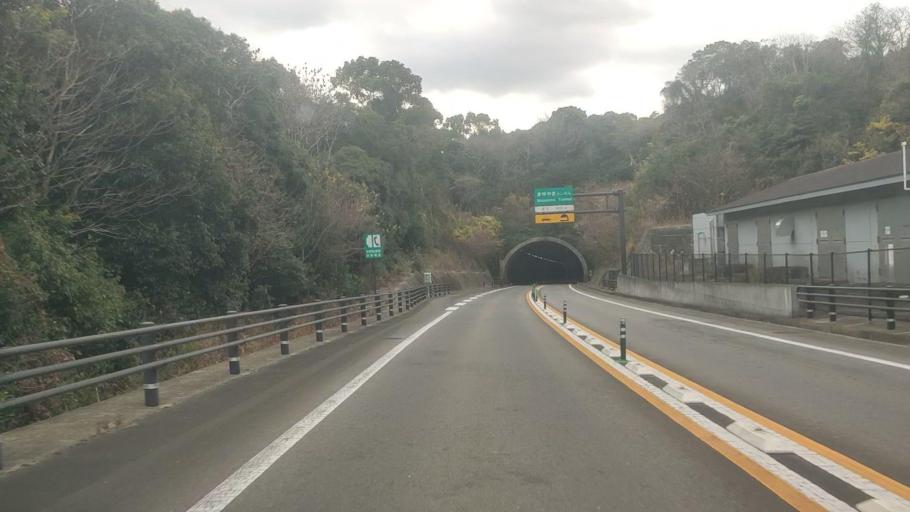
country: JP
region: Nagasaki
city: Shimabara
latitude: 32.7797
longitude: 130.3556
